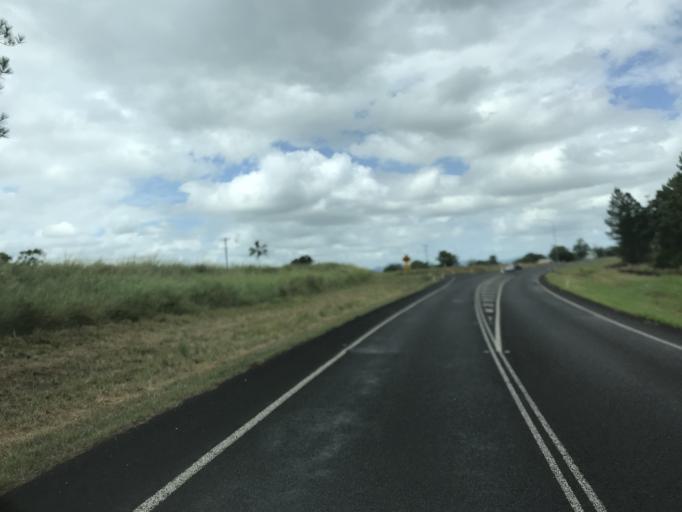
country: AU
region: Queensland
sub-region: Cassowary Coast
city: Innisfail
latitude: -17.5789
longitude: 145.9670
